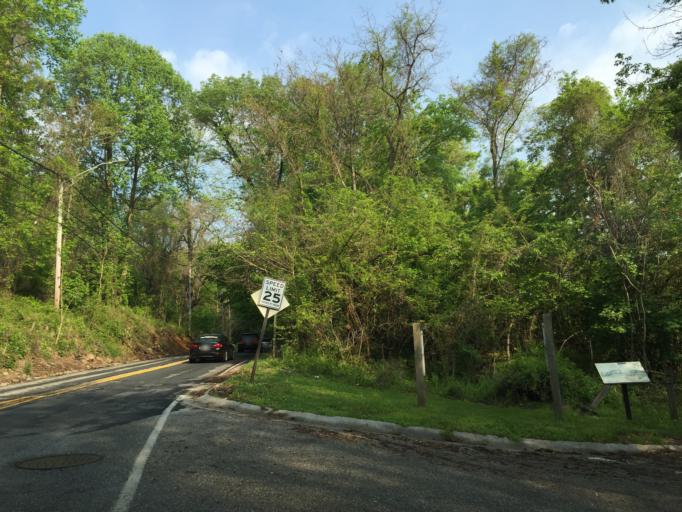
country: US
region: Maryland
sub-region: Baltimore County
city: Woodlawn
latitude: 39.3125
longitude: -76.6900
